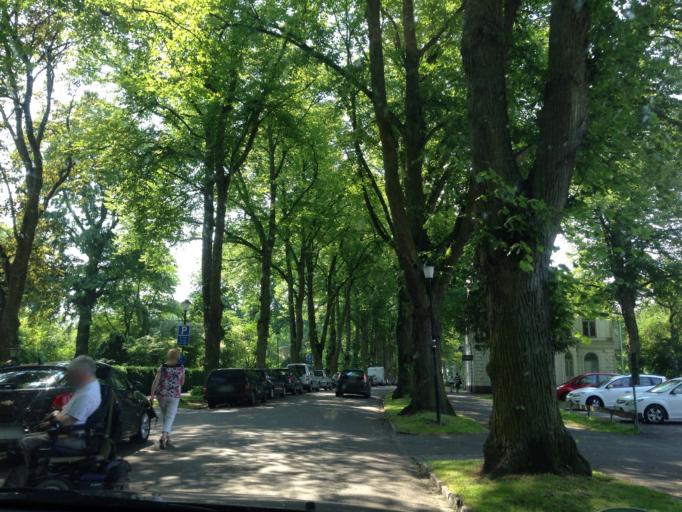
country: SE
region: Kalmar
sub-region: Kalmar Kommun
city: Kalmar
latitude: 56.6610
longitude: 16.3549
